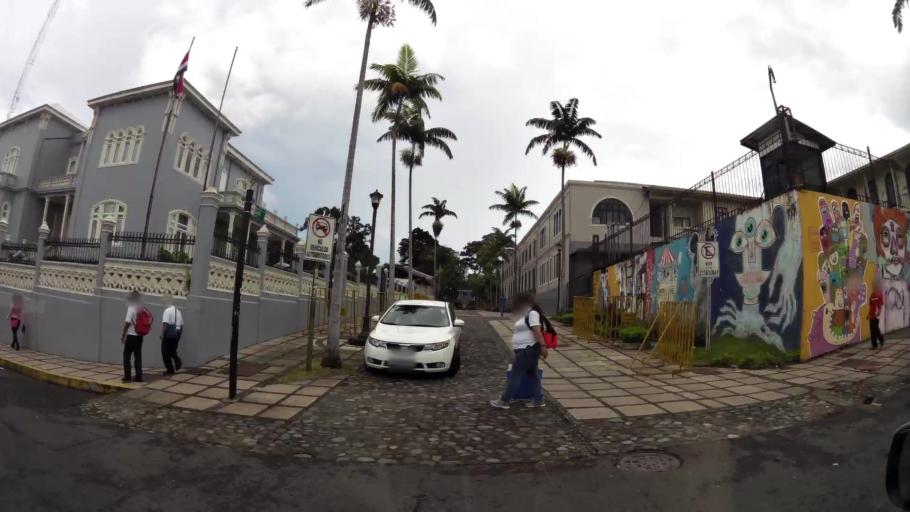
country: CR
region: San Jose
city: San Jose
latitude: 9.9334
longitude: -84.0708
